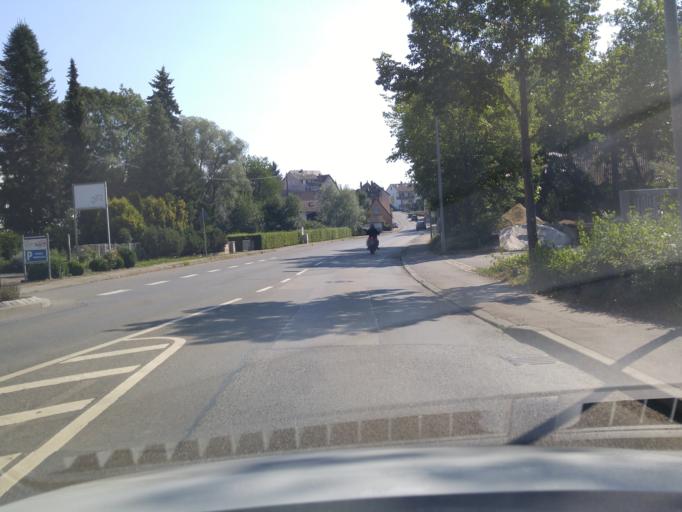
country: DE
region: Baden-Wuerttemberg
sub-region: Regierungsbezirk Stuttgart
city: Schlaitdorf
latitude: 48.6207
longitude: 9.2321
